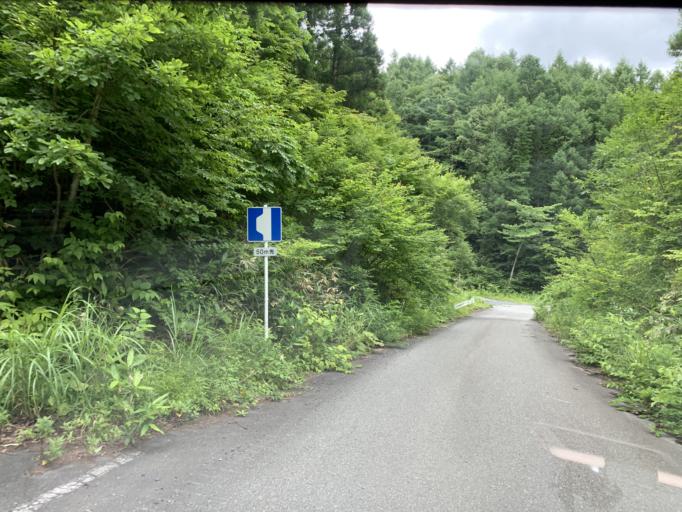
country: JP
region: Iwate
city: Ichinoseki
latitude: 38.9429
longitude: 140.8721
